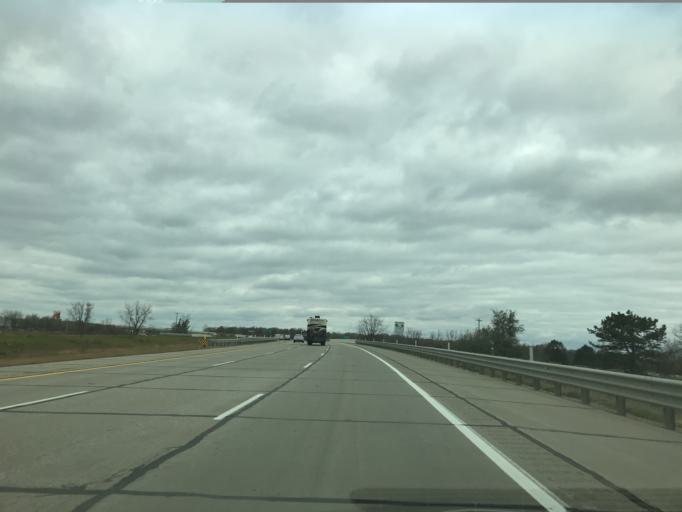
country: US
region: Michigan
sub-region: Clinton County
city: Wacousta
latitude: 42.7836
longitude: -84.6708
